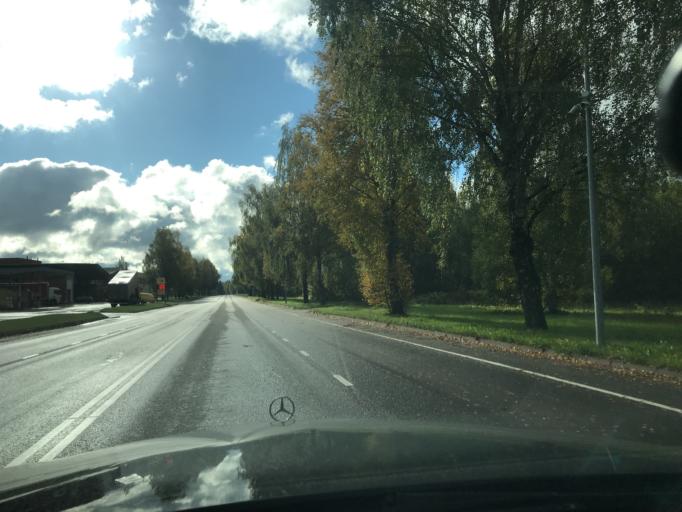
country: EE
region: Valgamaa
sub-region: Torva linn
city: Torva
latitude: 57.9917
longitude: 25.9389
